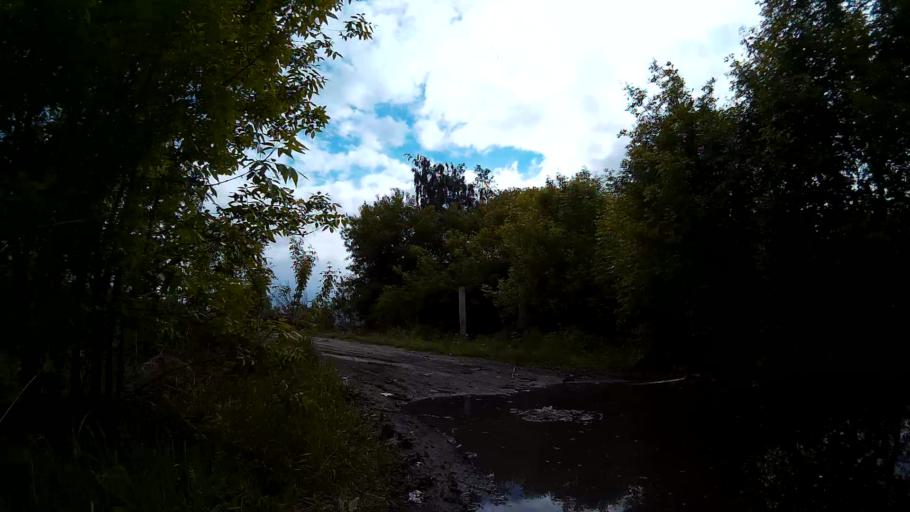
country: RU
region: Ulyanovsk
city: Novoul'yanovsk
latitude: 54.2367
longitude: 48.2955
